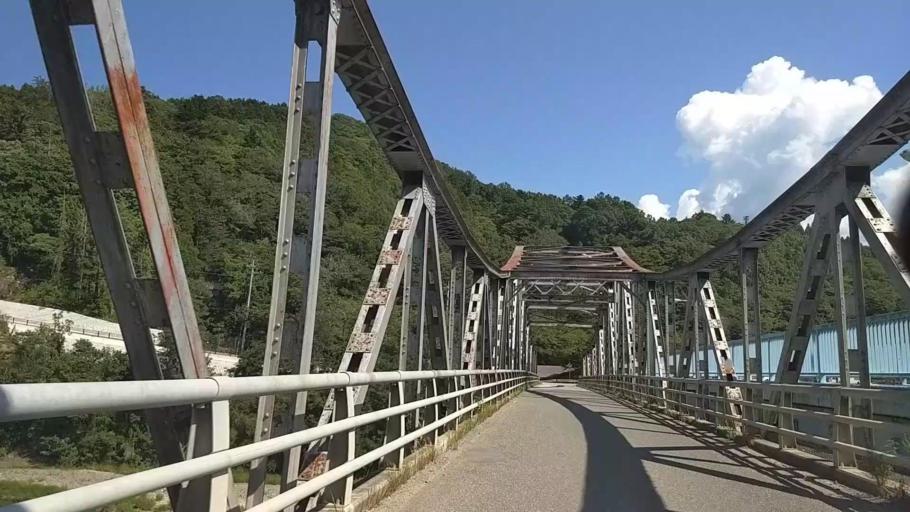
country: JP
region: Yamanashi
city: Ryuo
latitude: 35.4654
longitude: 138.4423
